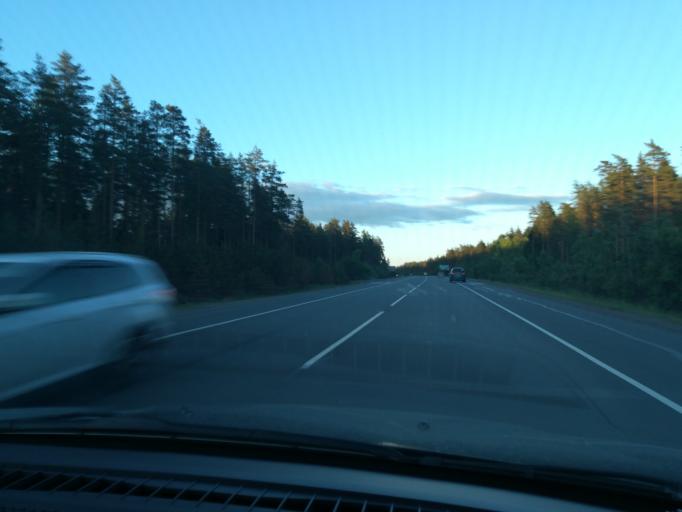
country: RU
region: Leningrad
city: Yakovlevo
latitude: 60.3606
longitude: 29.5778
